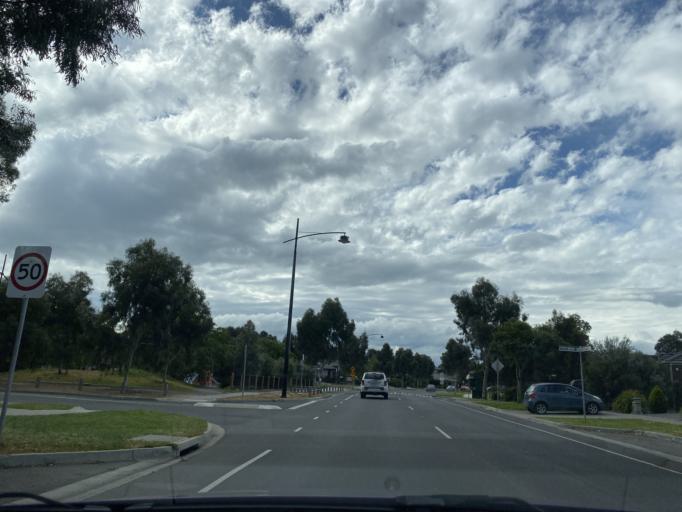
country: AU
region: Victoria
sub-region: Whittlesea
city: Mernda
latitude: -37.6035
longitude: 145.0878
